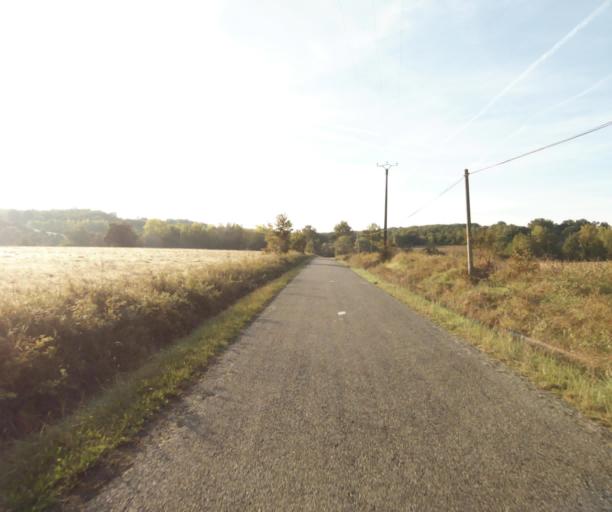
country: FR
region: Midi-Pyrenees
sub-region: Departement du Tarn-et-Garonne
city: Saint-Nauphary
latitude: 43.9459
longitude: 1.4415
